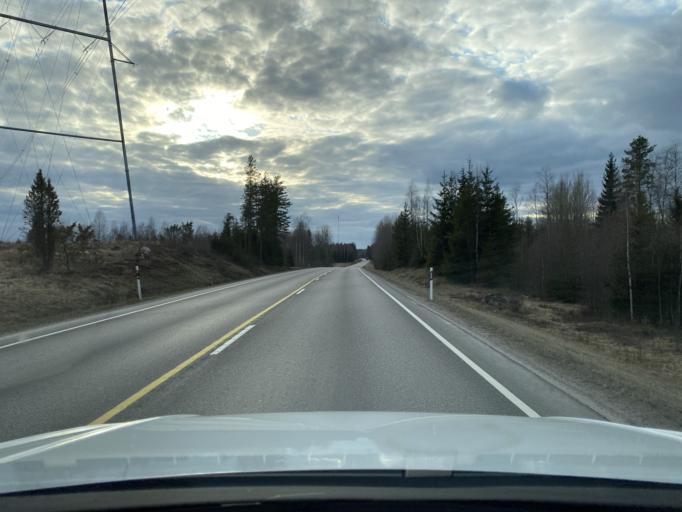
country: FI
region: Haeme
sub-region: Haemeenlinna
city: Renko
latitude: 60.7832
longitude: 24.1552
